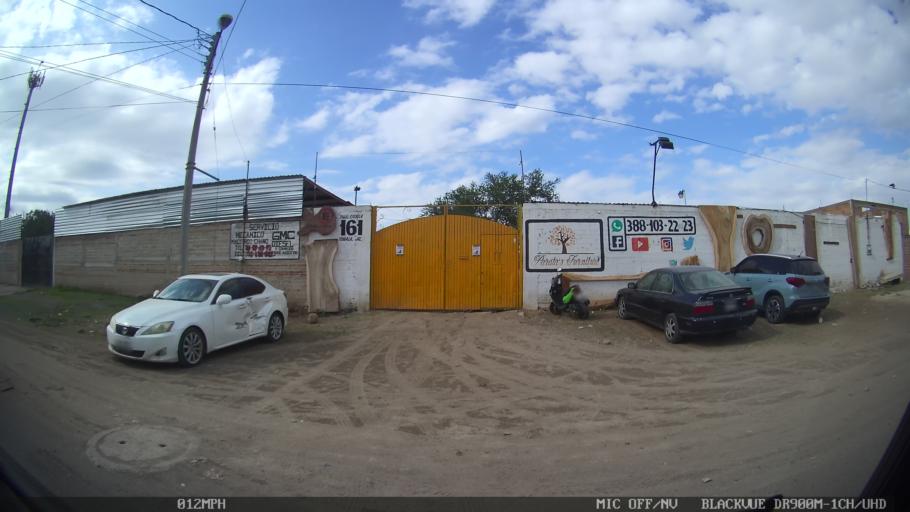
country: MX
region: Jalisco
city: Tonala
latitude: 20.6595
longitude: -103.2348
